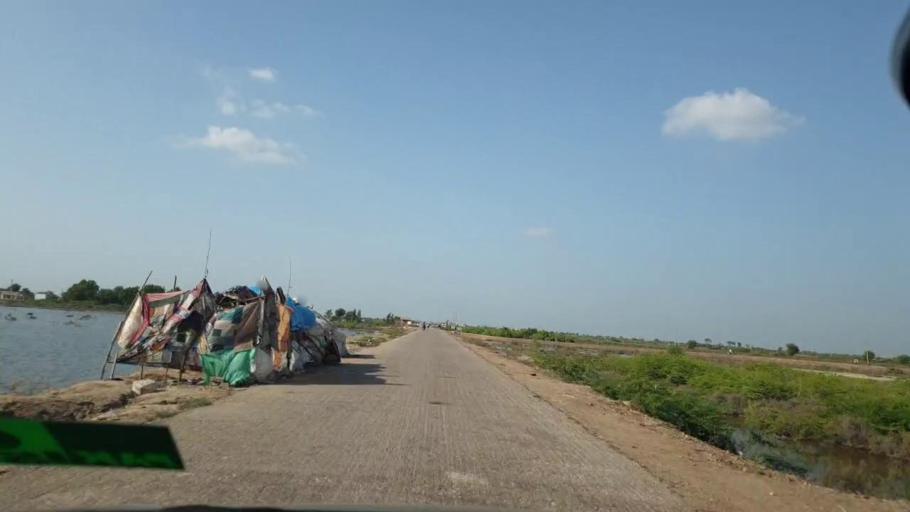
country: PK
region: Sindh
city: Naukot
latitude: 24.7389
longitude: 69.1983
